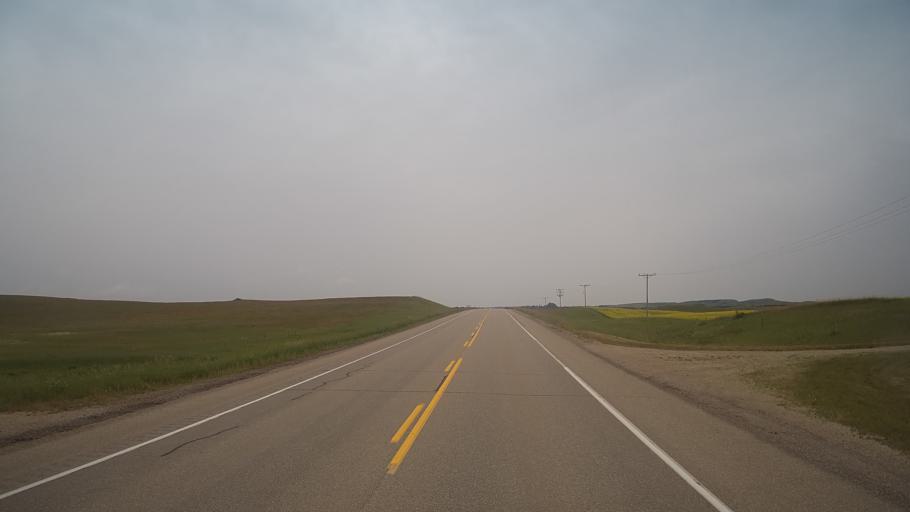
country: CA
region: Saskatchewan
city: Biggar
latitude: 52.0565
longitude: -107.8241
